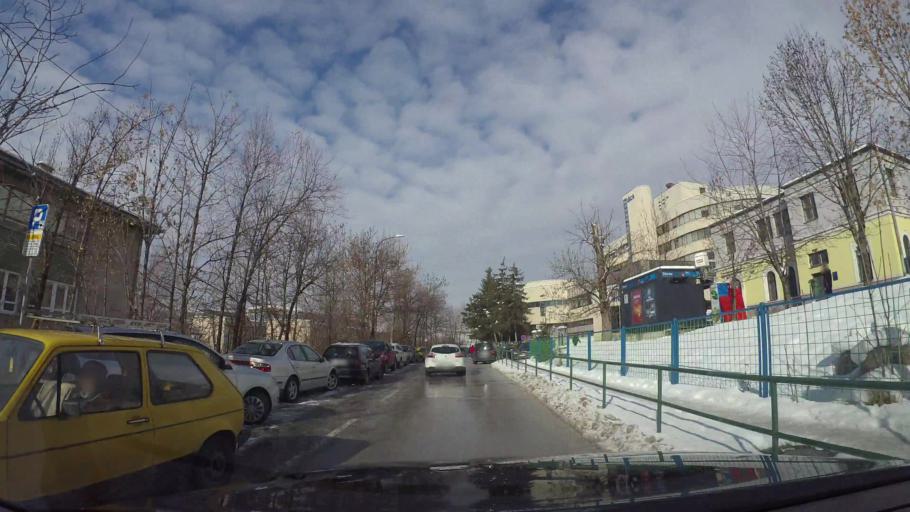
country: BA
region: Federation of Bosnia and Herzegovina
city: Kobilja Glava
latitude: 43.8691
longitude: 18.4140
